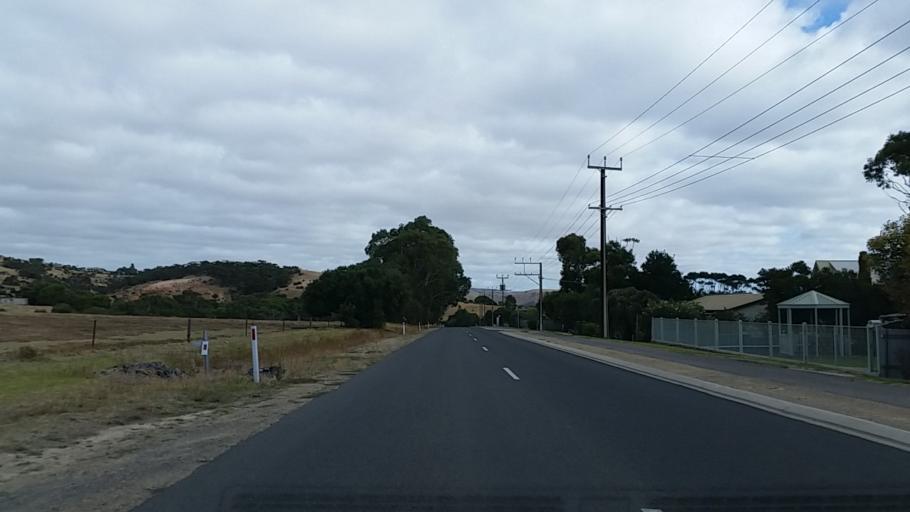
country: AU
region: South Australia
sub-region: Yankalilla
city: Normanville
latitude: -35.4286
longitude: 138.3264
